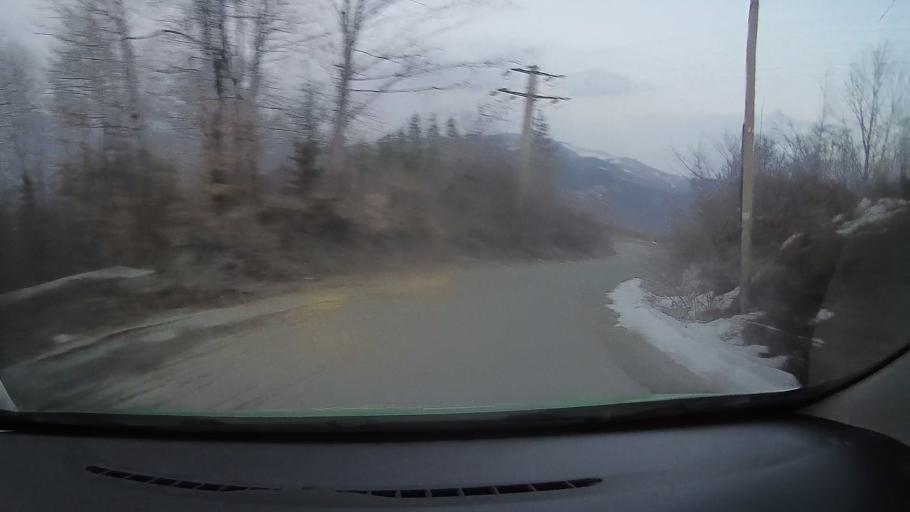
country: RO
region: Prahova
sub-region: Comuna Valea Doftanei
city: Tesila
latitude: 45.2924
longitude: 25.7061
